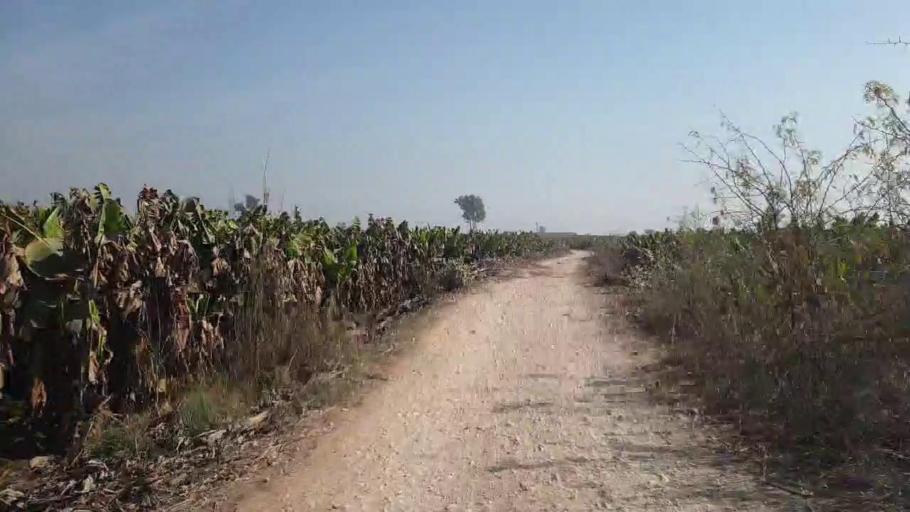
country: PK
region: Sindh
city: Tando Allahyar
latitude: 25.4071
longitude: 68.7554
